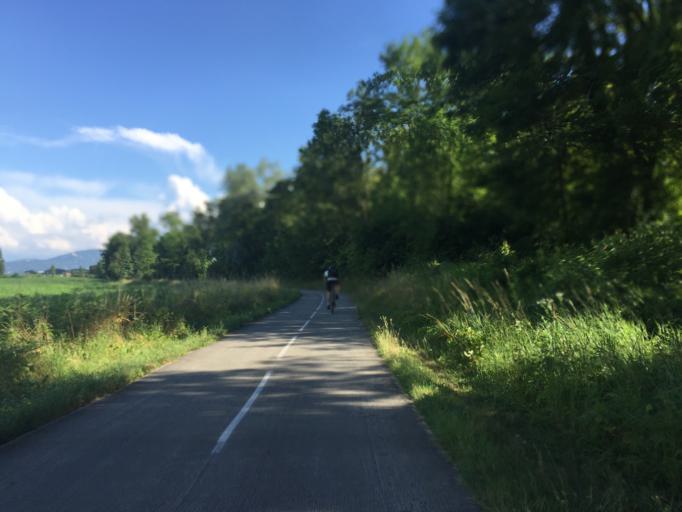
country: FR
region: Rhone-Alpes
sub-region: Departement de la Savoie
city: Le Bourget-du-Lac
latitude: 45.6332
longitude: 5.8710
